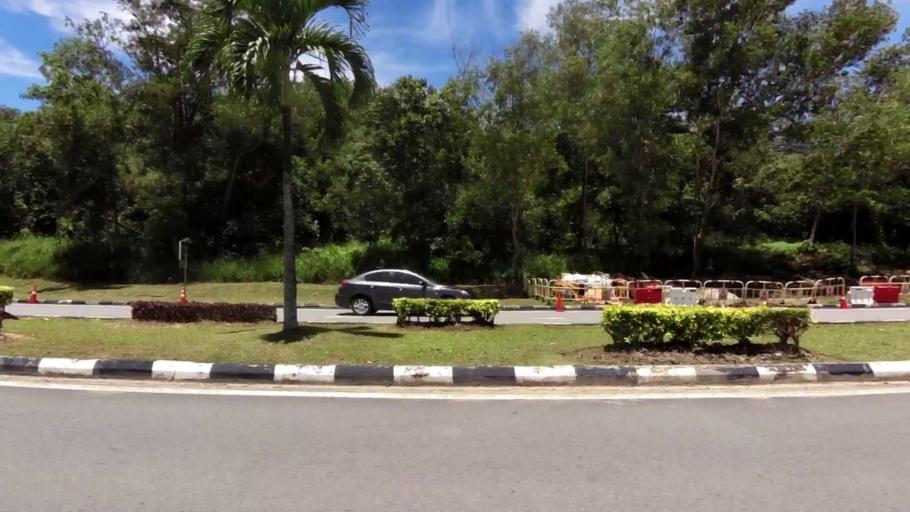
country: BN
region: Brunei and Muara
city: Bandar Seri Begawan
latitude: 4.9212
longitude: 114.9418
